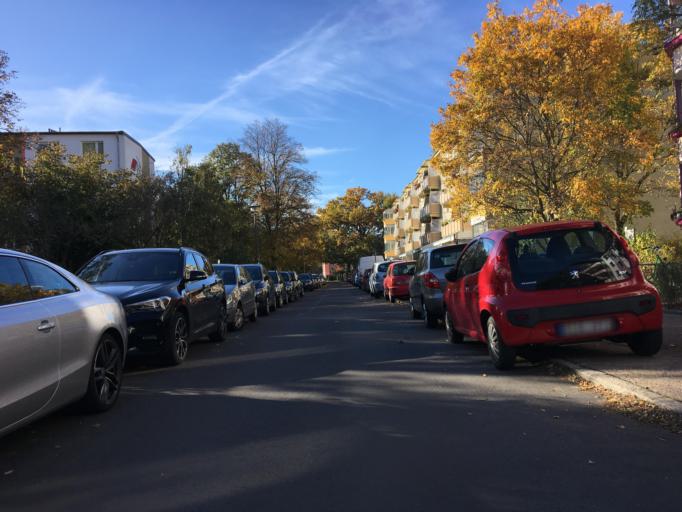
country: DE
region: Berlin
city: Friedrichshagen
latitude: 52.4489
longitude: 13.6311
